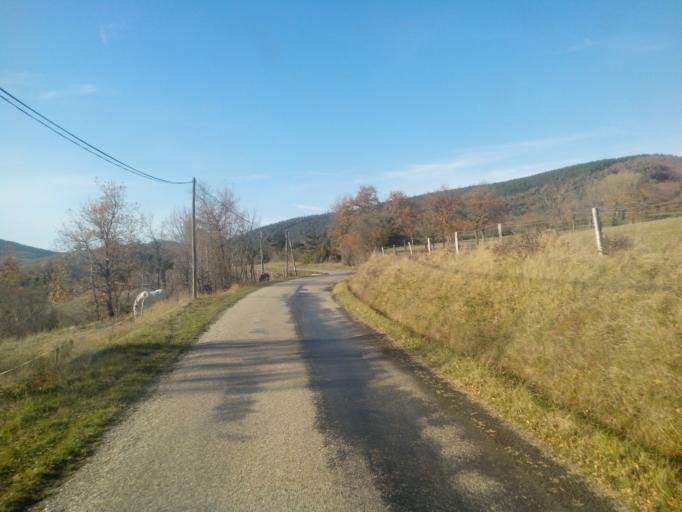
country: FR
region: Languedoc-Roussillon
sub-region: Departement des Pyrenees-Orientales
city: Saint-Paul-de-Fenouillet
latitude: 42.8641
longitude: 2.4258
